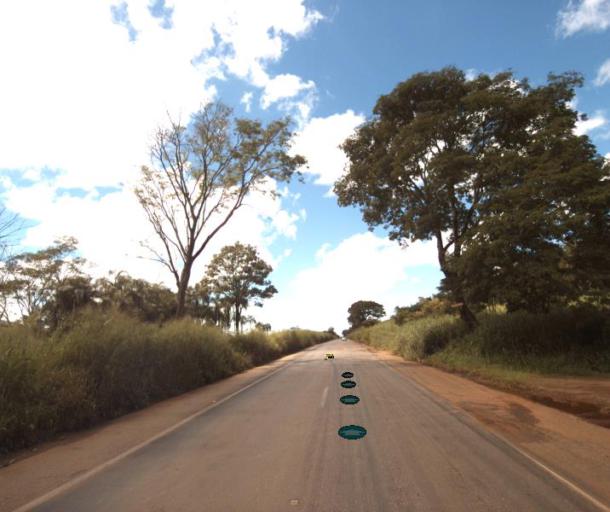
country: BR
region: Goias
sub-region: Petrolina De Goias
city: Petrolina de Goias
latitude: -15.9874
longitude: -49.1549
